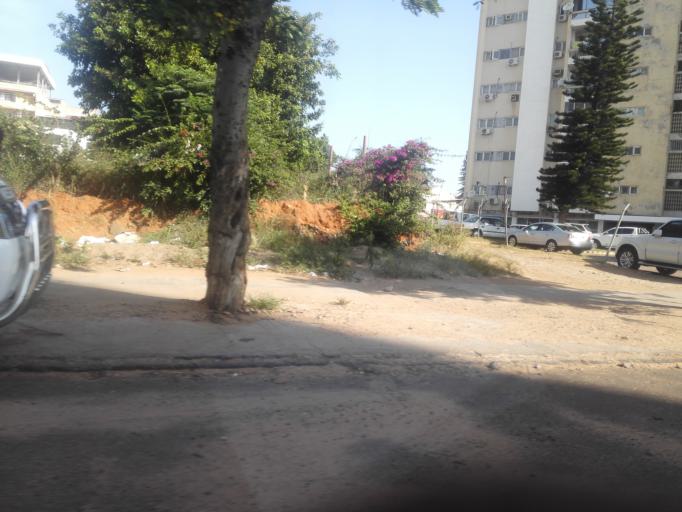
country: MZ
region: Maputo City
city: Maputo
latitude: -25.9545
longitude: 32.5875
